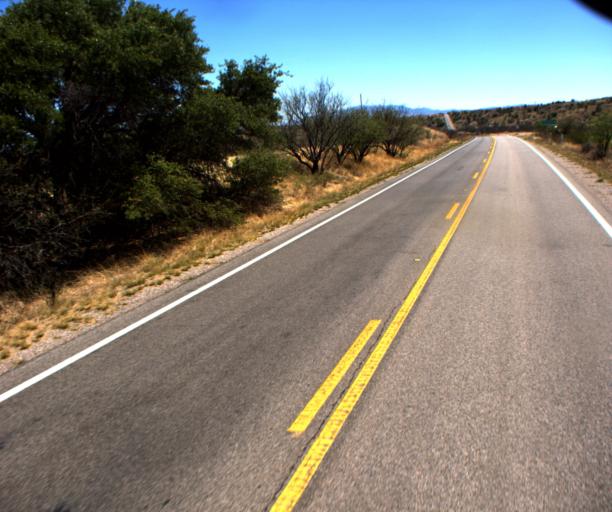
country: US
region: Arizona
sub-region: Pima County
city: Corona de Tucson
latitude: 31.7874
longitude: -110.6976
